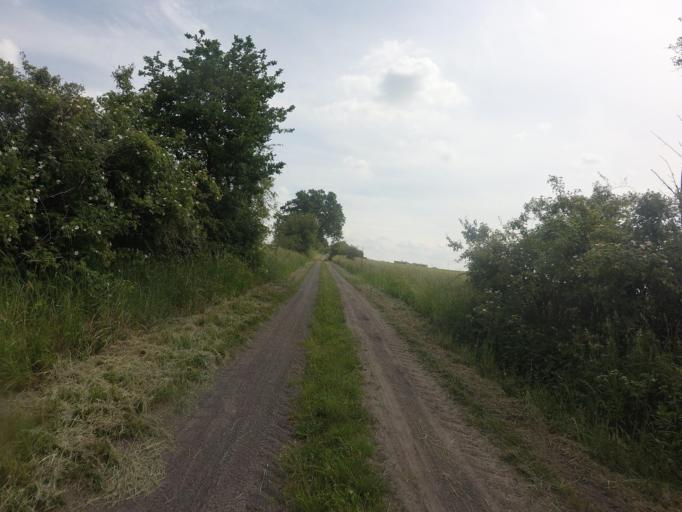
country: PL
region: West Pomeranian Voivodeship
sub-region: Powiat choszczenski
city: Recz
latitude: 53.2874
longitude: 15.4818
